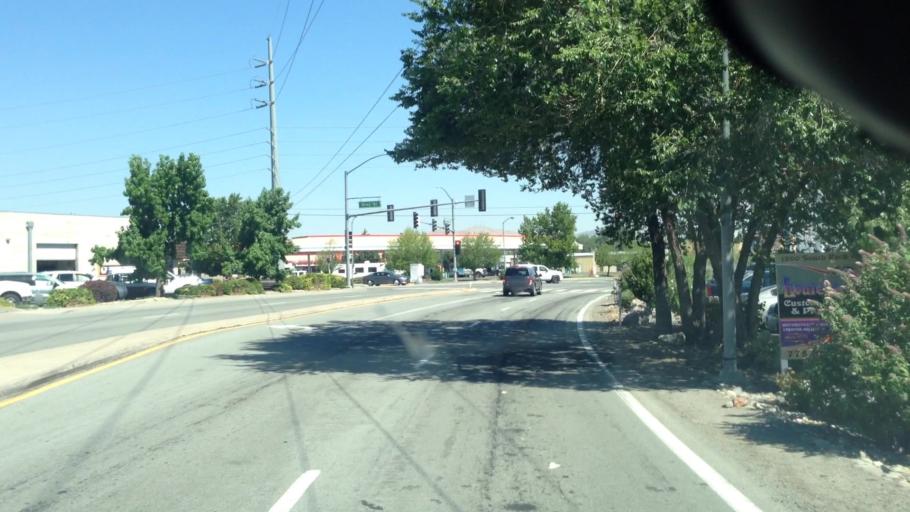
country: US
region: Nevada
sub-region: Washoe County
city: Sparks
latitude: 39.5227
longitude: -119.7664
